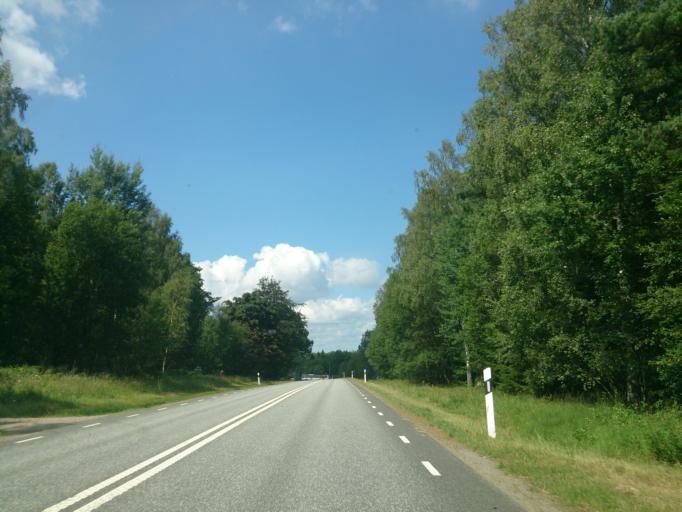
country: SE
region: Joenkoeping
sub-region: Varnamo Kommun
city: Bredaryd
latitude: 57.1738
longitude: 13.7211
